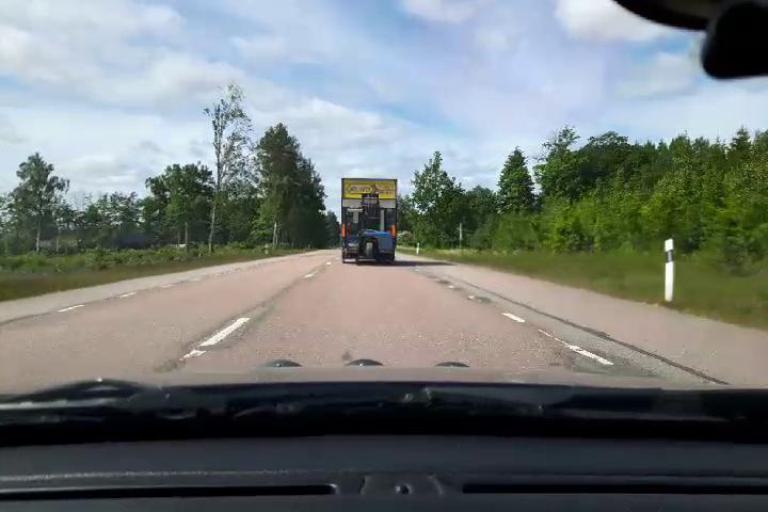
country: SE
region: Uppsala
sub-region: Osthammars Kommun
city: Bjorklinge
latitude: 60.1093
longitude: 17.5373
